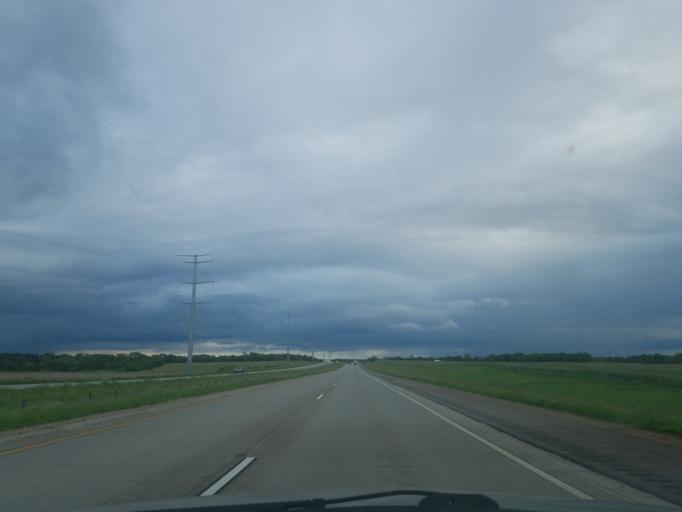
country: US
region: Minnesota
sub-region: Stearns County
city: Saint Augusta
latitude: 45.4544
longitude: -94.1233
